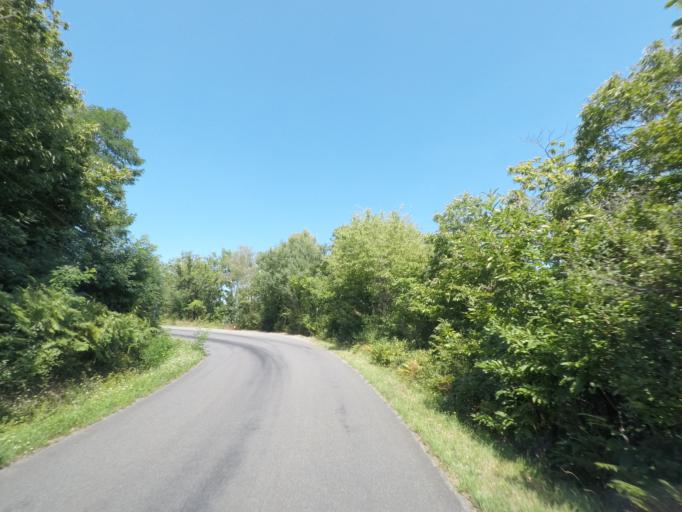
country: FR
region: Midi-Pyrenees
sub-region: Departement de l'Aveyron
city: Livinhac-le-Haut
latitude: 44.6099
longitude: 2.2266
